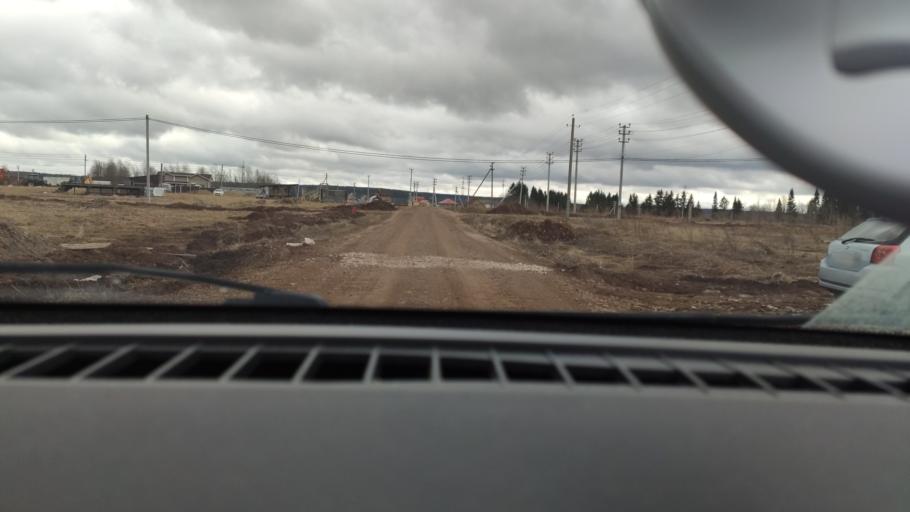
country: RU
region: Perm
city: Ferma
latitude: 57.9476
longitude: 56.3405
